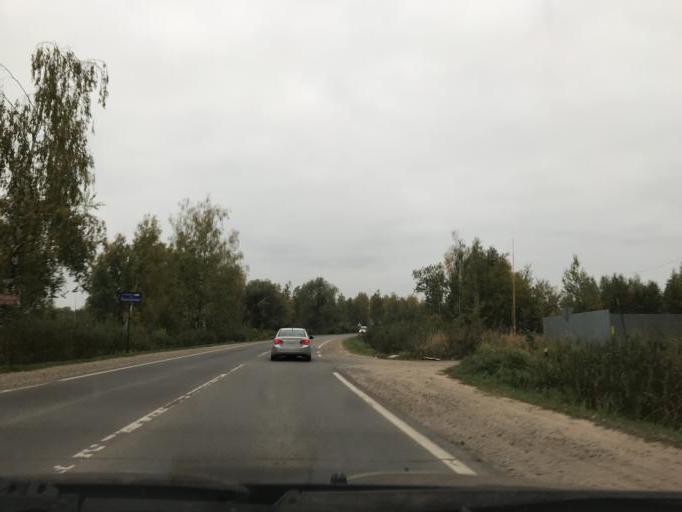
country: RU
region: Kaluga
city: Kaluga
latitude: 54.6173
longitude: 36.2833
